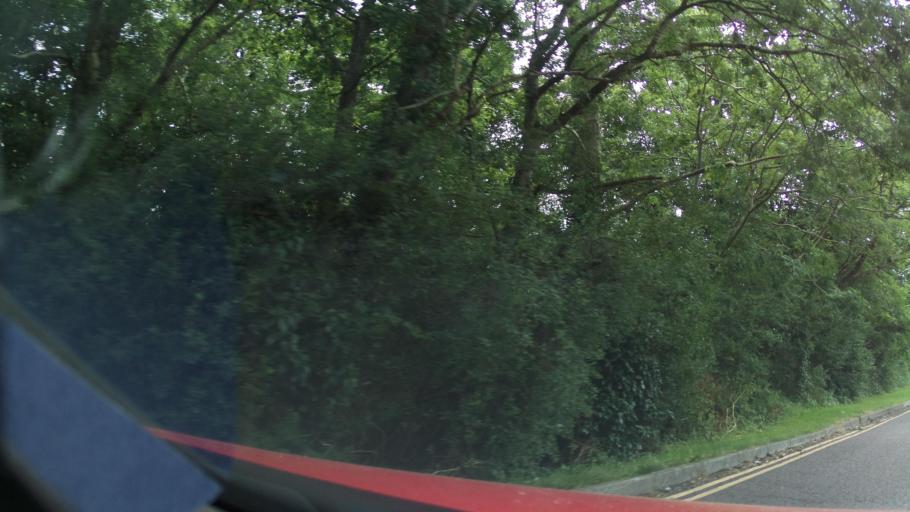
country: GB
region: England
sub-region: Wiltshire
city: Lydiard Tregoze
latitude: 51.5584
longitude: -1.8423
